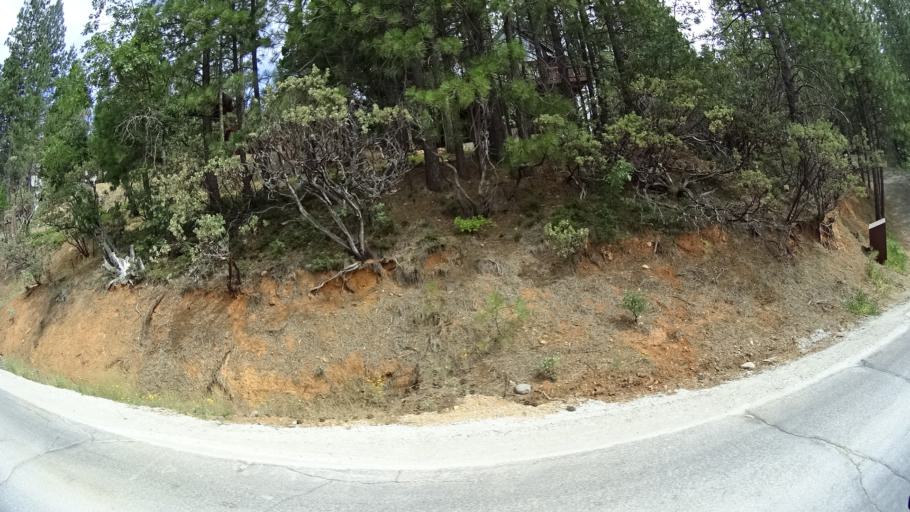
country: US
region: California
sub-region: Calaveras County
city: Arnold
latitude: 38.2435
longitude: -120.3423
